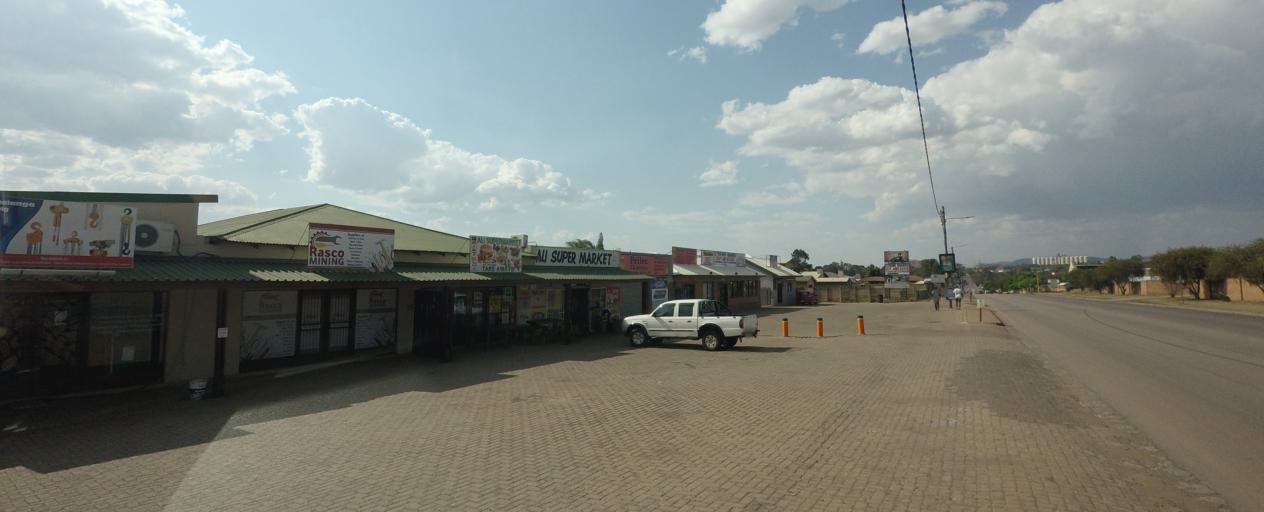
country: ZA
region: Mpumalanga
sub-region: Ehlanzeni District
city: Lydenburg
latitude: -25.1065
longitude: 30.4505
